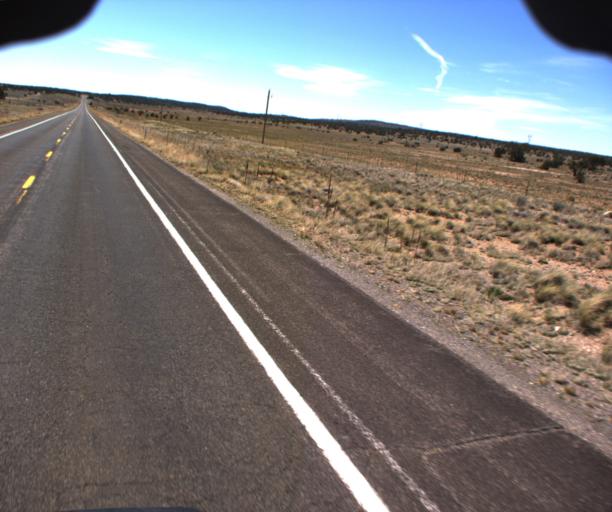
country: US
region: Arizona
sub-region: Mohave County
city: Peach Springs
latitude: 35.5540
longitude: -113.3272
